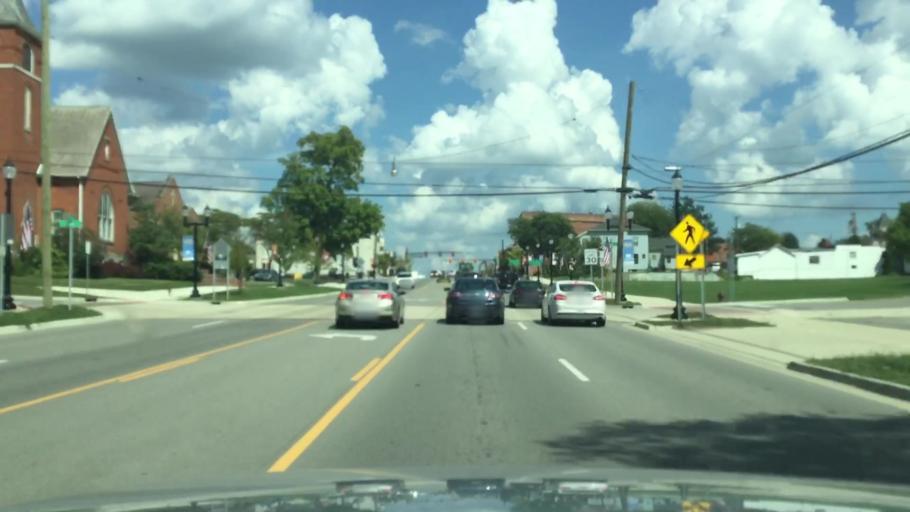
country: US
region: Michigan
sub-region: Washtenaw County
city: Saline
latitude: 42.1655
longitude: -83.7839
